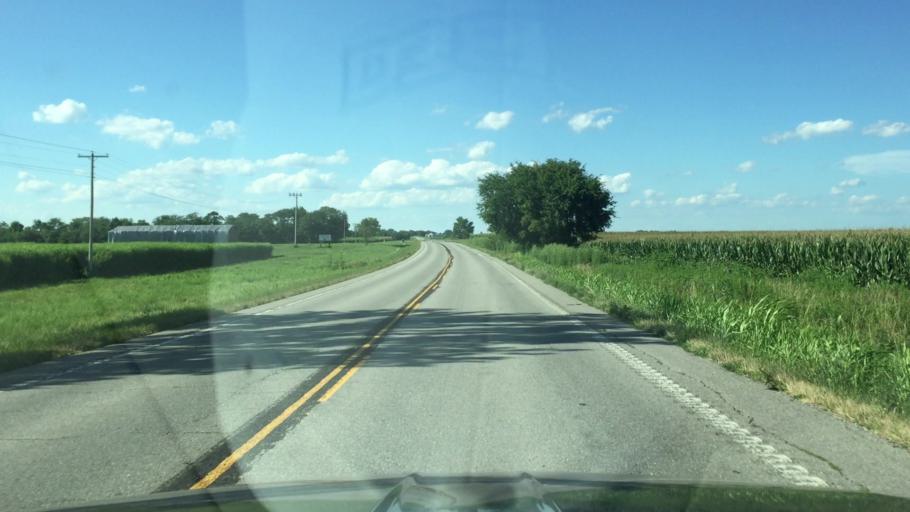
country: US
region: Missouri
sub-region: Moniteau County
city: Tipton
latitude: 38.5912
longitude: -92.7891
